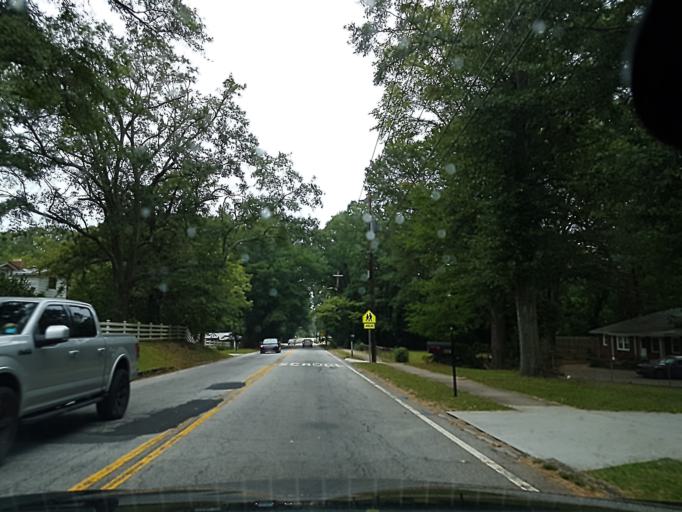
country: US
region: Georgia
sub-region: DeKalb County
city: Scottdale
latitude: 33.8030
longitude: -84.2670
